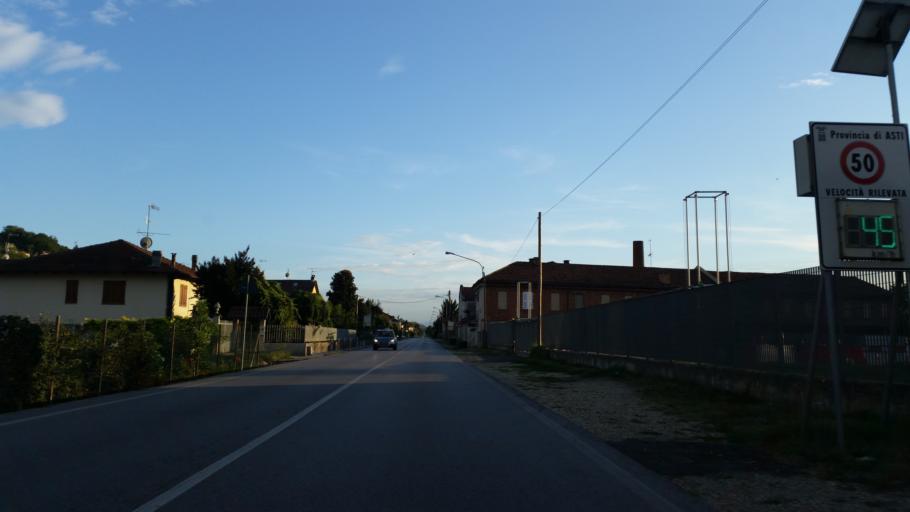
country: IT
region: Piedmont
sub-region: Provincia di Asti
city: Mongardino
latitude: 44.8640
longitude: 8.2071
